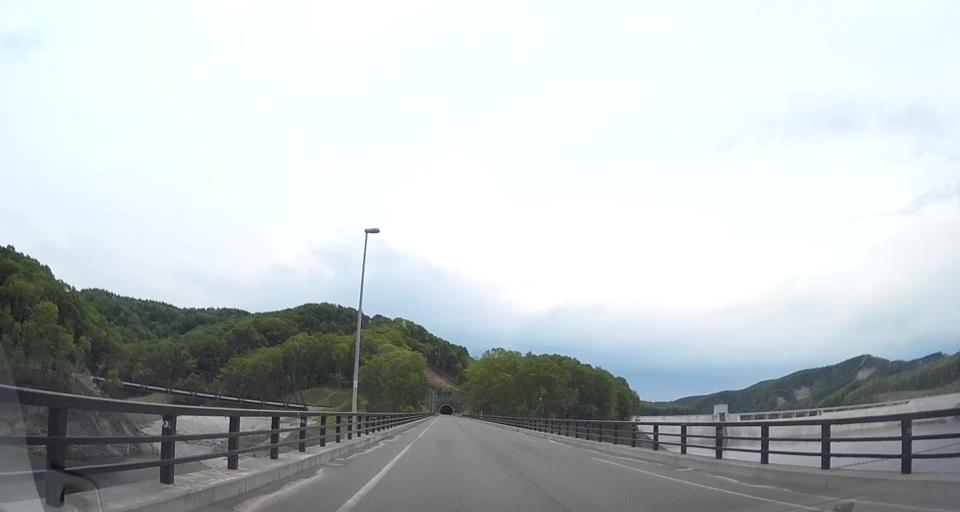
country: JP
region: Hokkaido
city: Chitose
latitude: 42.7667
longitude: 142.0001
